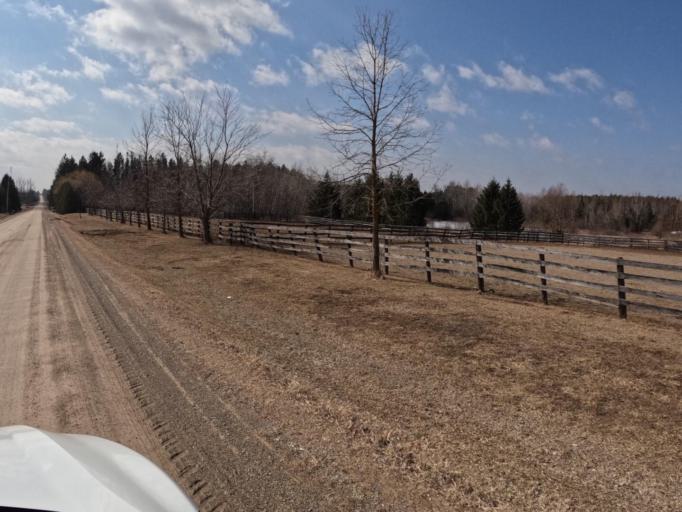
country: CA
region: Ontario
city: Orangeville
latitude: 43.9115
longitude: -80.2534
